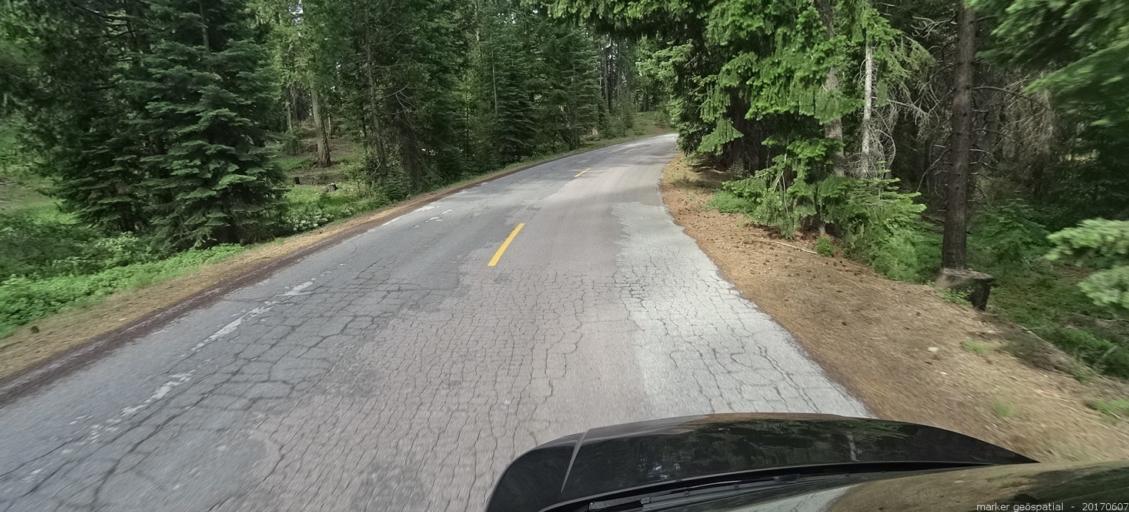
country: US
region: California
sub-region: Shasta County
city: Burney
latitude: 41.1869
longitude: -121.7054
